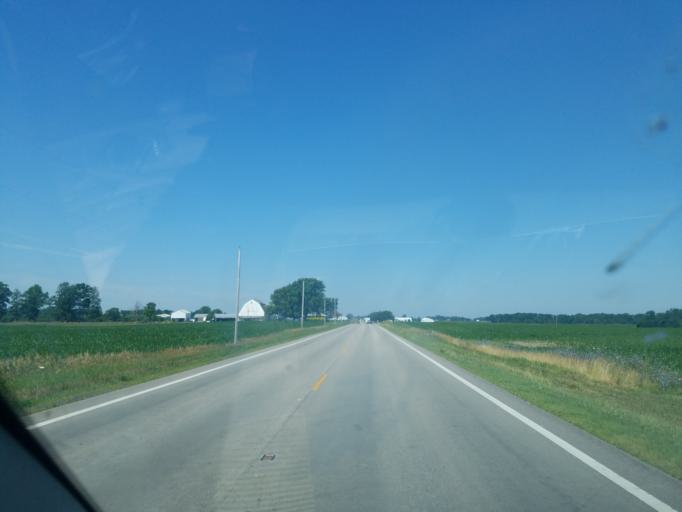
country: US
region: Ohio
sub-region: Shelby County
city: Botkins
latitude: 40.4388
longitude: -84.2311
